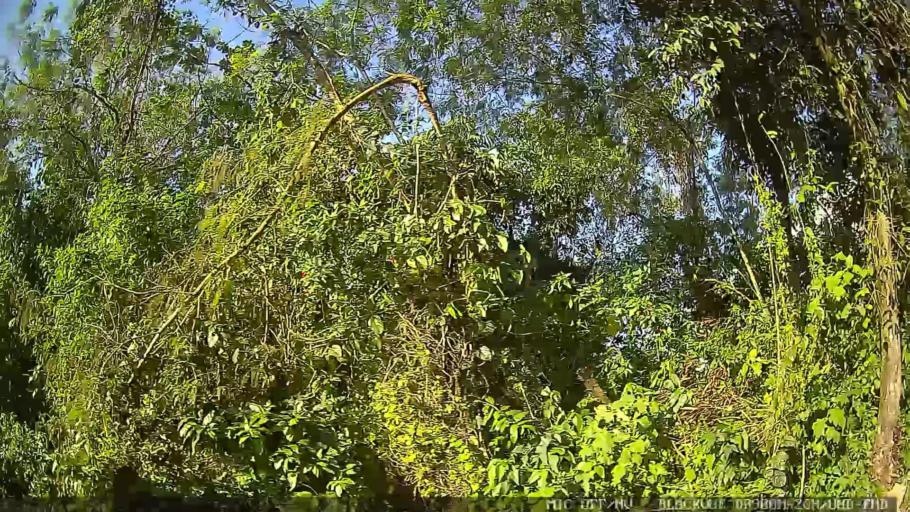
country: BR
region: Sao Paulo
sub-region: Guaruja
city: Guaruja
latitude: -23.9725
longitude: -46.2712
